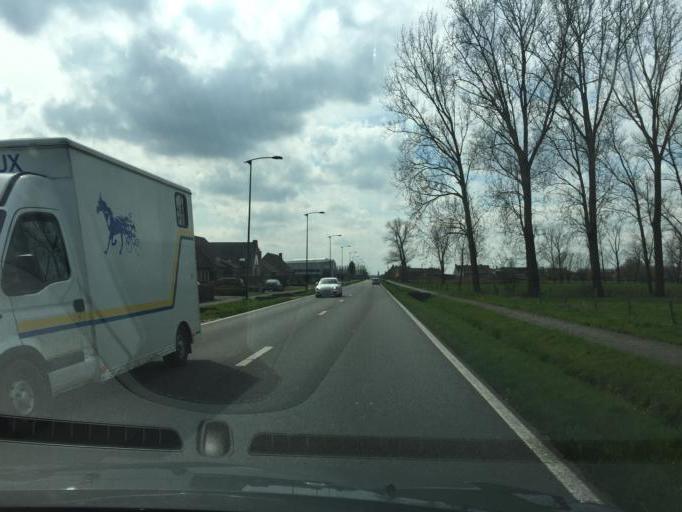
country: BE
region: Flanders
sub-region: Provincie Oost-Vlaanderen
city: Aalter
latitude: 51.0670
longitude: 3.4343
